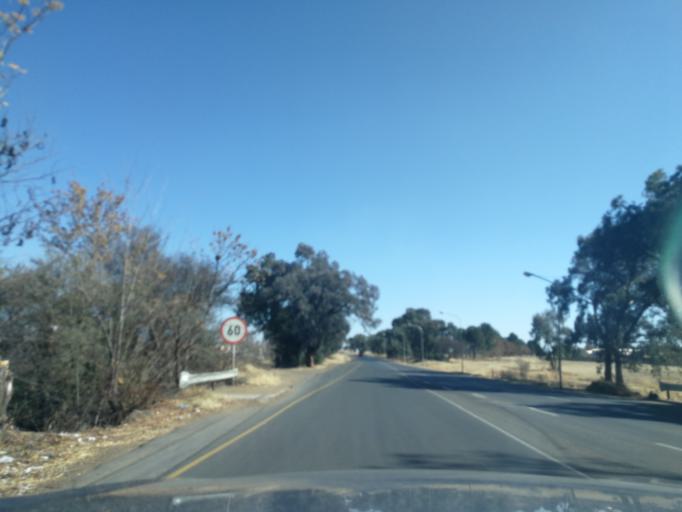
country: ZA
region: Orange Free State
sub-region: Fezile Dabi District Municipality
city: Kroonstad
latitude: -27.6475
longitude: 27.2281
